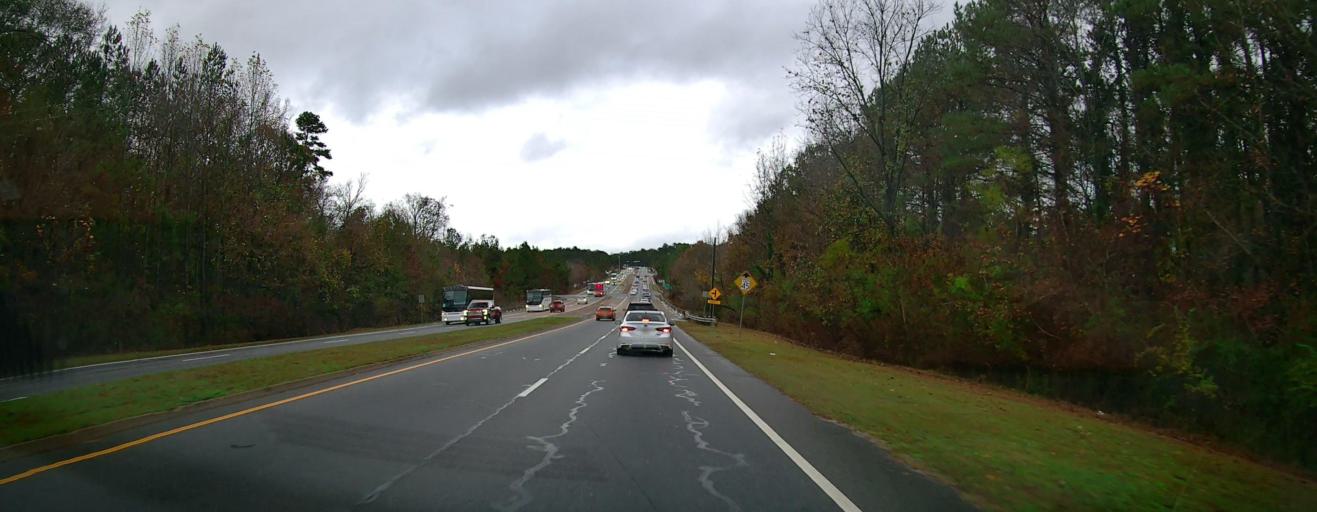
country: US
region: Georgia
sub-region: Oconee County
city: Watkinsville
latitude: 33.9095
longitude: -83.4043
